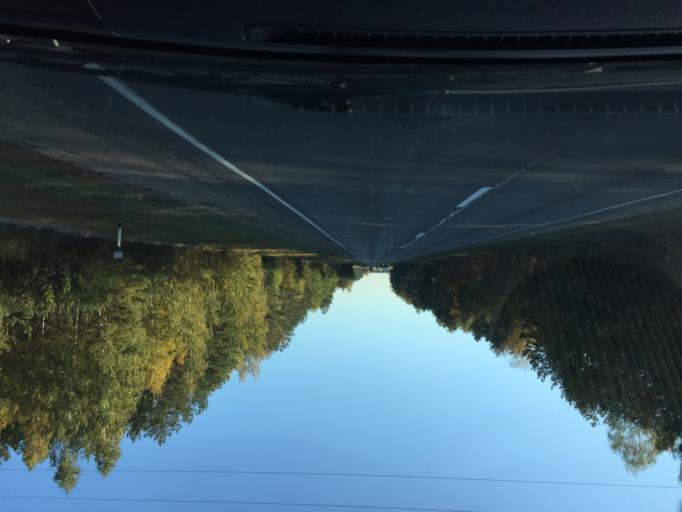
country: BY
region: Brest
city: Luninyets
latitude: 52.2707
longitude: 26.9943
